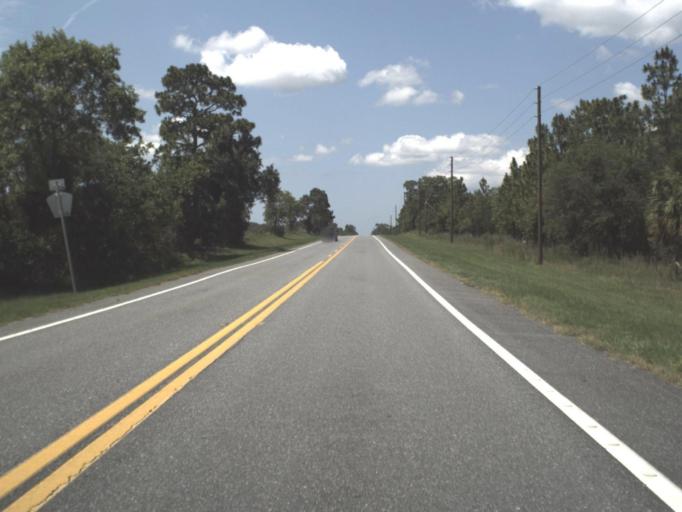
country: US
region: Florida
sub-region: Levy County
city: Williston Highlands
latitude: 29.2448
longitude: -82.5554
